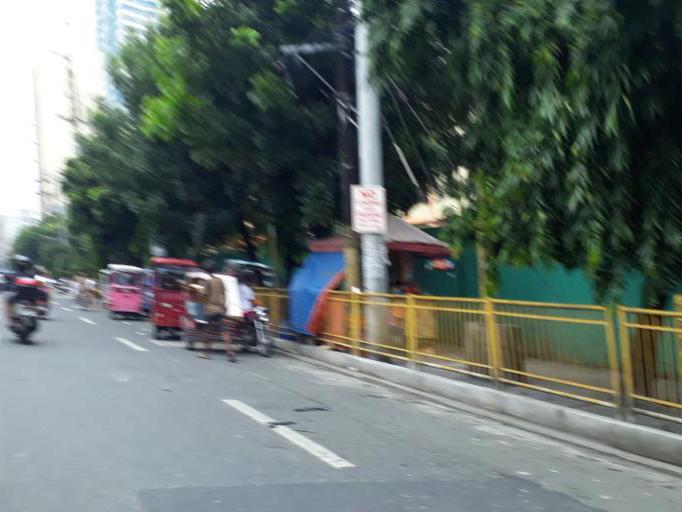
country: PH
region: Metro Manila
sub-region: City of Manila
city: Manila
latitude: 14.6061
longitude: 120.9750
